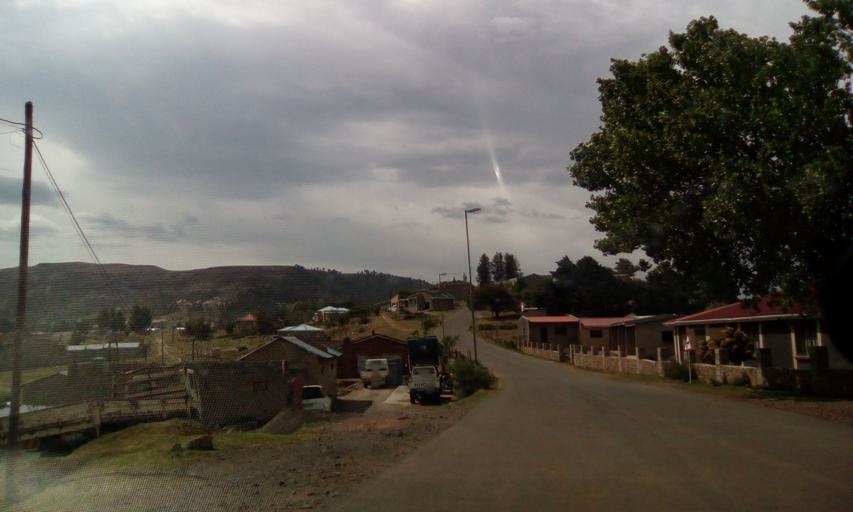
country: LS
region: Qacha's Nek
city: Qacha's Nek
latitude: -30.1150
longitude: 28.6777
